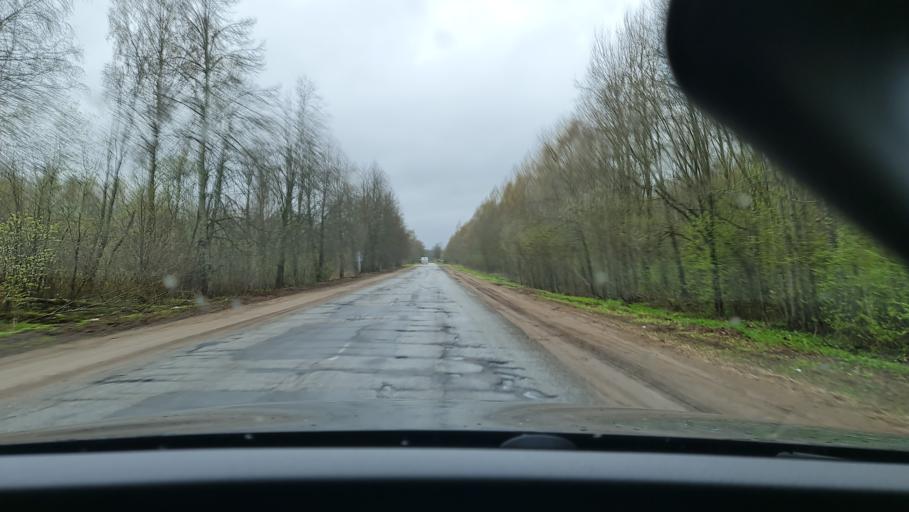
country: RU
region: Novgorod
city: Demyansk
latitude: 57.6694
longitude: 32.5418
